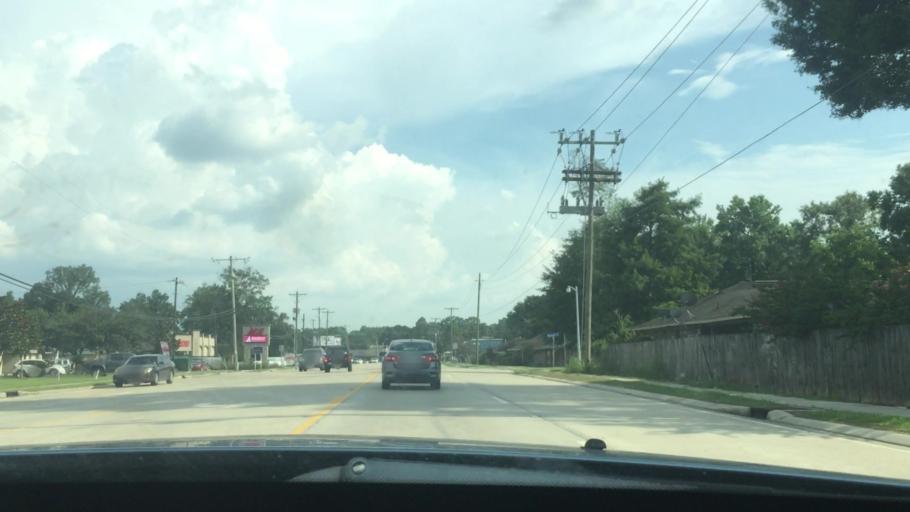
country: US
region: Louisiana
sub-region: East Baton Rouge Parish
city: Shenandoah
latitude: 30.4331
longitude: -91.0245
